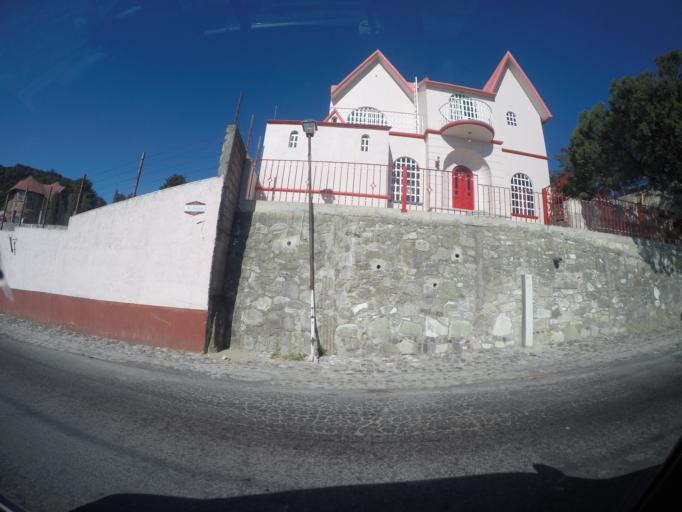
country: MX
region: Hidalgo
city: Mineral del Monte
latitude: 20.1377
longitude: -98.6824
